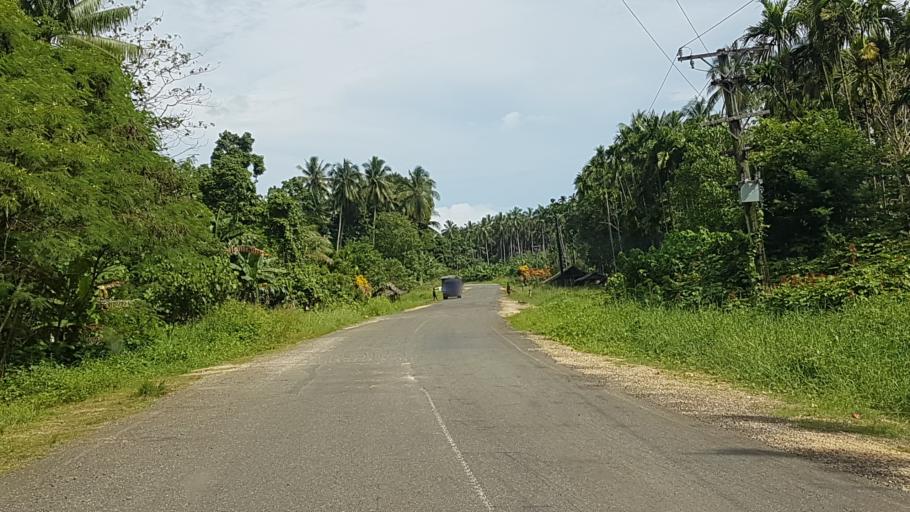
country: PG
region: Madang
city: Madang
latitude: -5.0339
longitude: 145.7981
